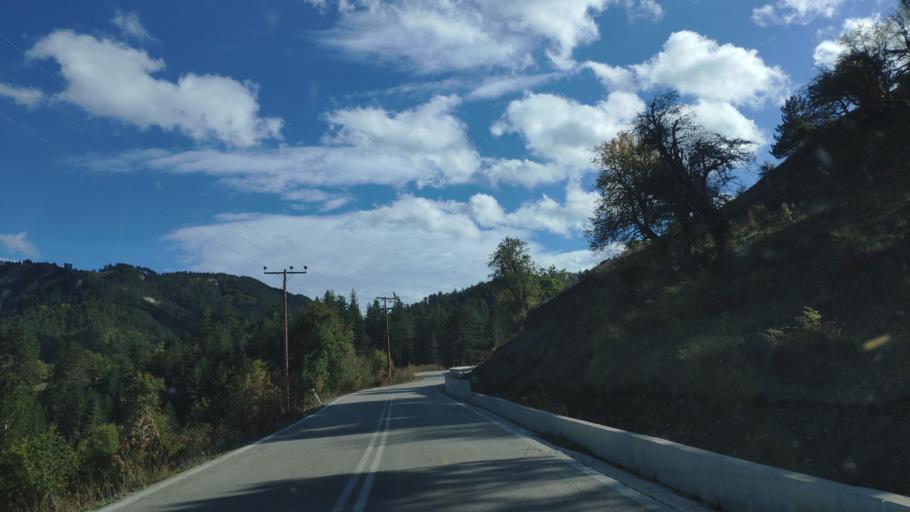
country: AL
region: Korce
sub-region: Rrethi i Devollit
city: Miras
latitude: 40.4009
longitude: 20.8824
